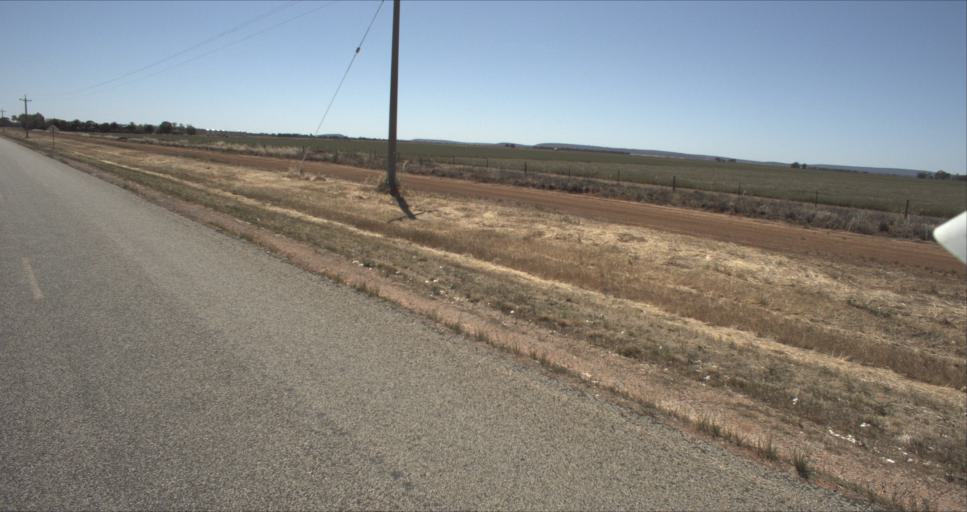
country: AU
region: New South Wales
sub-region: Leeton
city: Leeton
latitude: -34.4564
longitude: 146.2950
